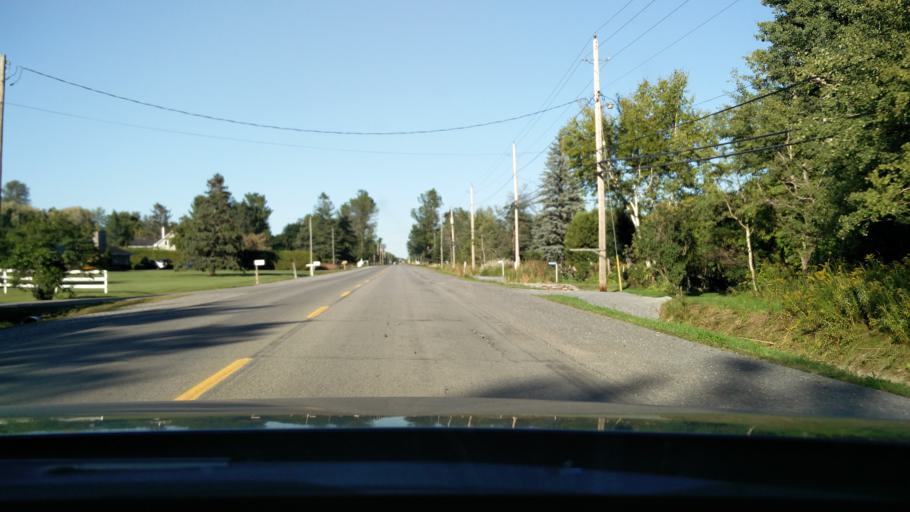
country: CA
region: Ontario
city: Bells Corners
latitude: 45.1784
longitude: -75.8637
